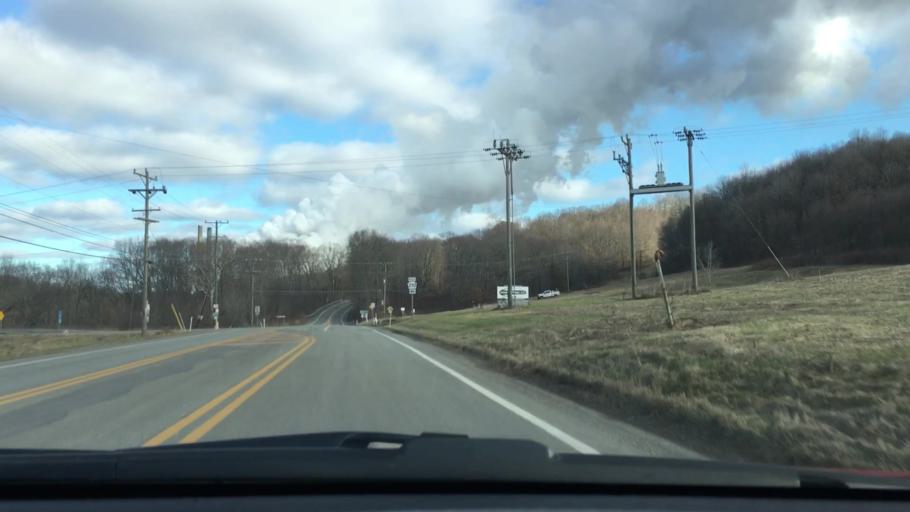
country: US
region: Pennsylvania
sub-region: Westmoreland County
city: Avonmore
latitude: 40.6395
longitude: -79.3530
